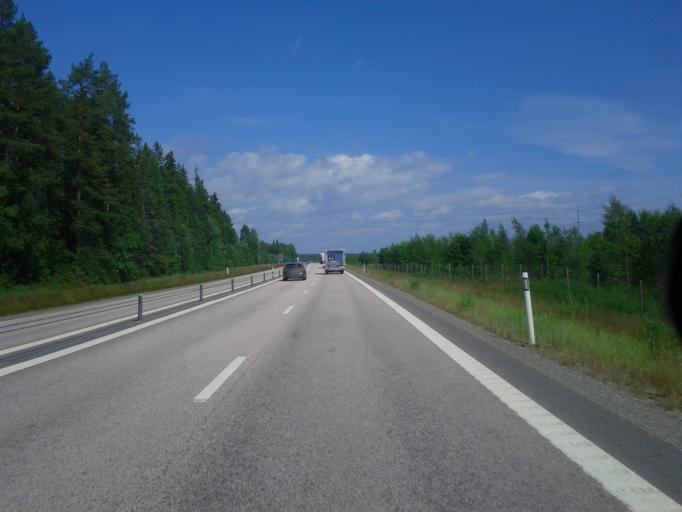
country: SE
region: Vaesterbotten
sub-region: Nordmalings Kommun
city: Nordmaling
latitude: 63.5562
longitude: 19.4223
